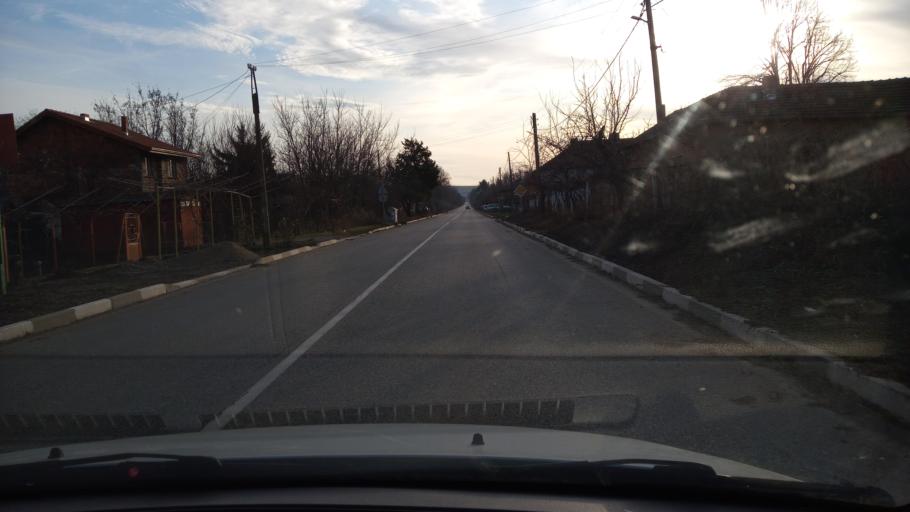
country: BG
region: Pleven
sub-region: Obshtina Pleven
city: Slavyanovo
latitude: 43.5612
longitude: 24.8691
